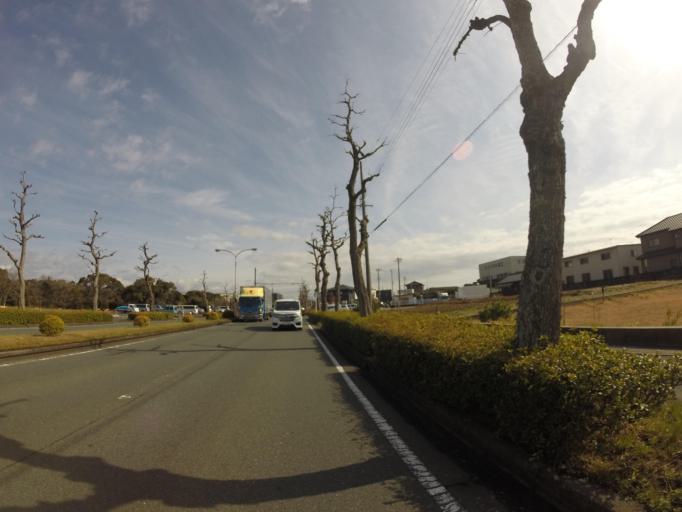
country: JP
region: Shizuoka
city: Hamamatsu
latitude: 34.7710
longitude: 137.6912
